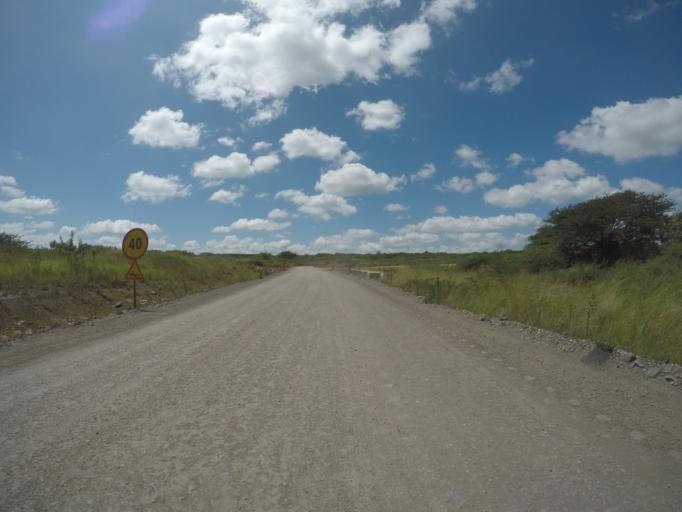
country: ZA
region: KwaZulu-Natal
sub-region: uThungulu District Municipality
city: Empangeni
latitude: -28.6614
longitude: 31.7805
